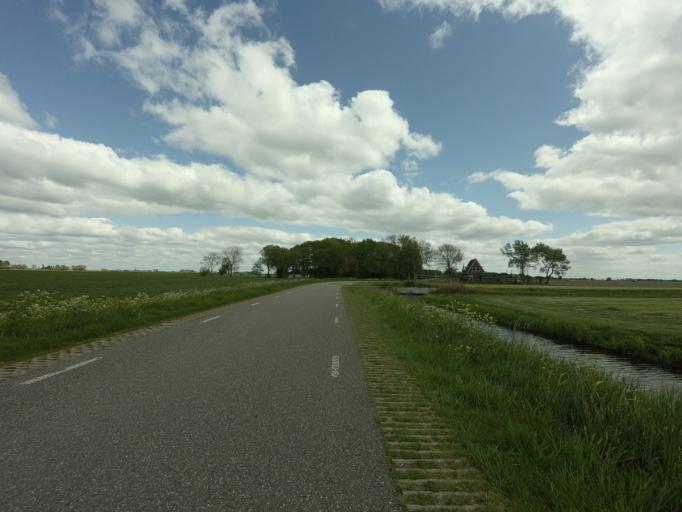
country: NL
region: Friesland
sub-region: Sudwest Fryslan
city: Bolsward
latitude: 53.0916
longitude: 5.5393
